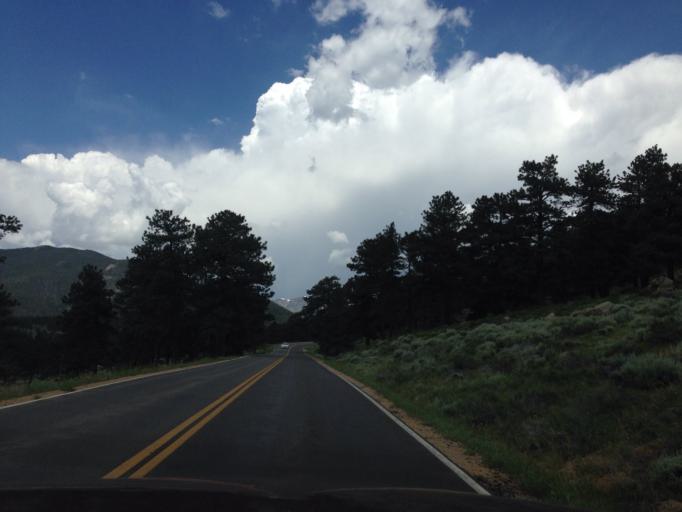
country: US
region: Colorado
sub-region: Larimer County
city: Estes Park
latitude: 40.3748
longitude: -105.5939
